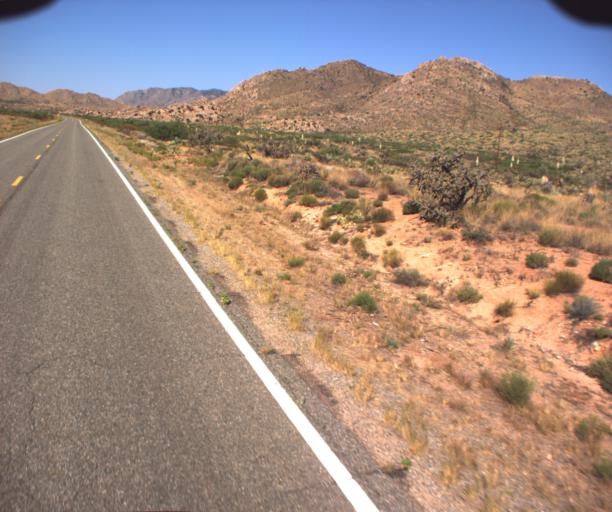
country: US
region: Arizona
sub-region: Graham County
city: Swift Trail Junction
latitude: 32.5790
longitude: -109.7099
